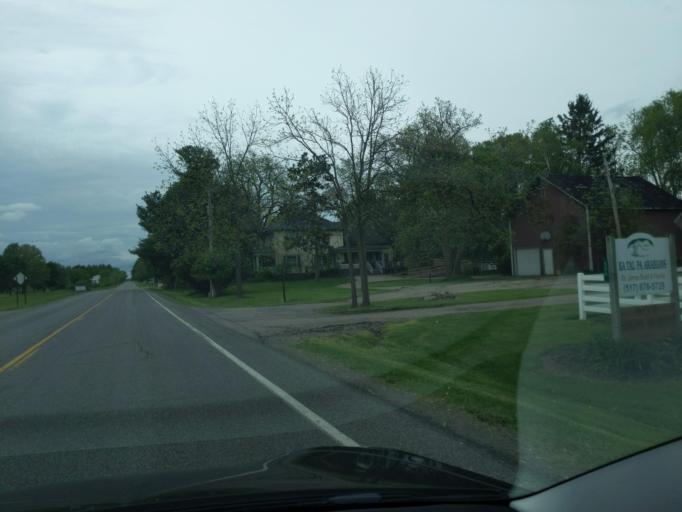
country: US
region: Michigan
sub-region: Ingham County
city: Mason
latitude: 42.5990
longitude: -84.4443
